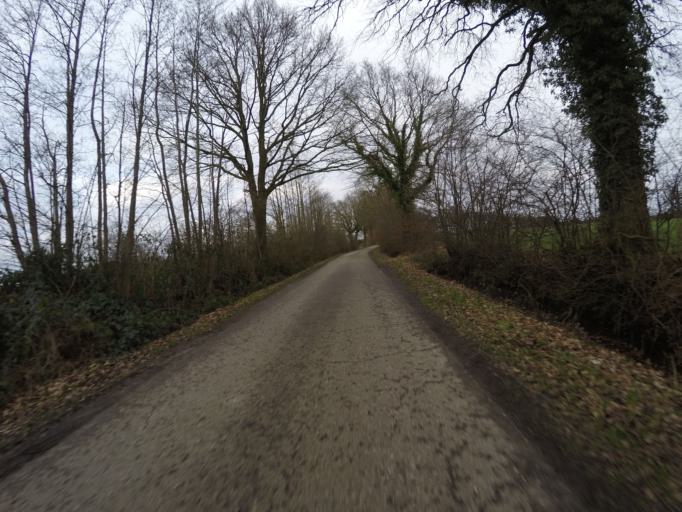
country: DE
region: Schleswig-Holstein
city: Alveslohe
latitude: 53.7991
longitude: 9.9038
